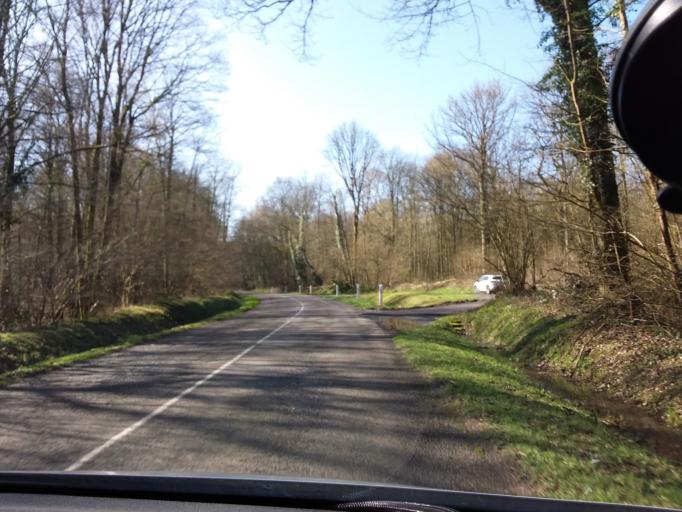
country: FR
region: Picardie
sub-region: Departement de l'Aisne
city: Hirson
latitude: 49.9468
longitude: 4.0765
